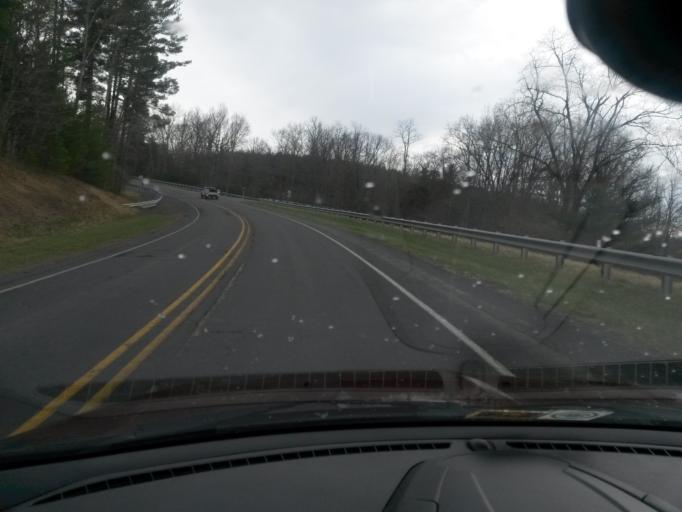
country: US
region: Virginia
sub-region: Bath County
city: Warm Springs
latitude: 38.0868
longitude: -79.7879
